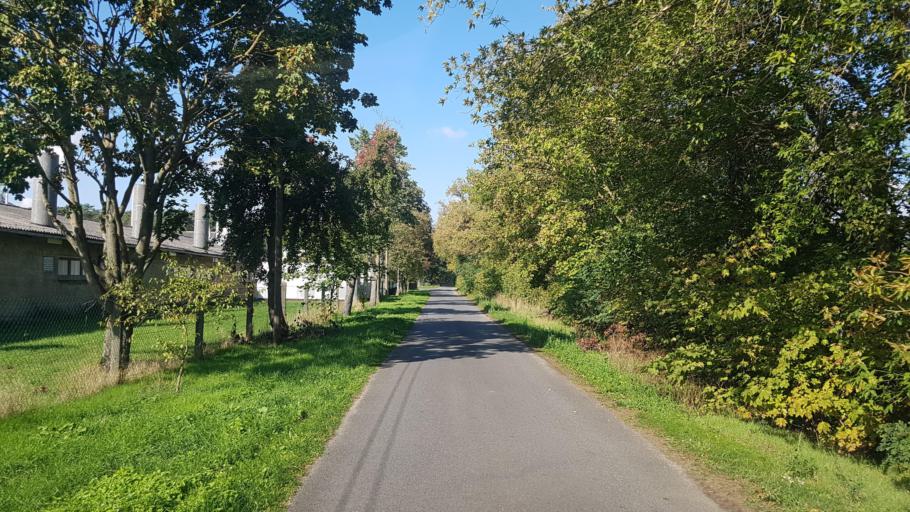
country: DE
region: Brandenburg
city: Ihlow
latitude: 51.8515
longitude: 13.2666
